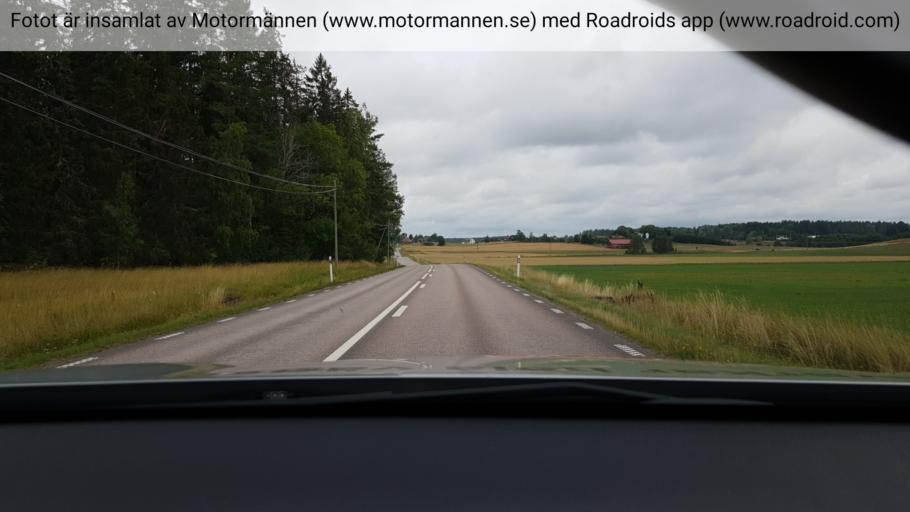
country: SE
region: Soedermanland
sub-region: Gnesta Kommun
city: Gnesta
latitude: 59.0506
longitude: 17.2633
